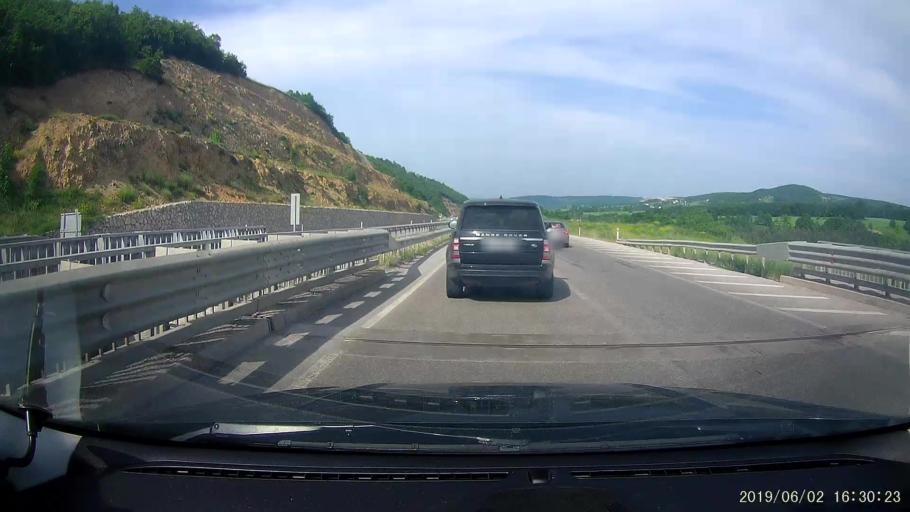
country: TR
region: Samsun
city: Ladik
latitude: 41.0248
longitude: 35.8815
